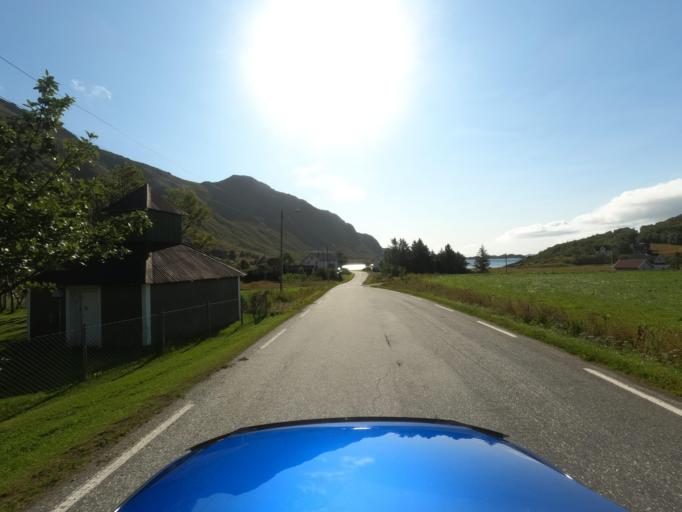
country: NO
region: Nordland
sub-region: Vestvagoy
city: Leknes
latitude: 68.1020
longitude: 13.6556
